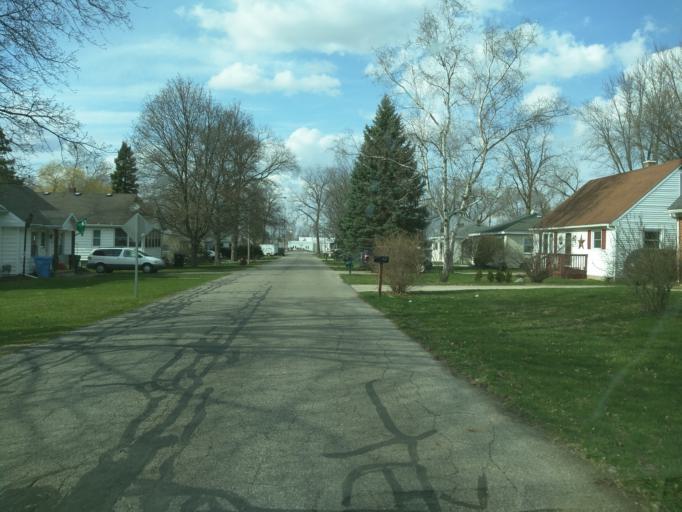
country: US
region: Michigan
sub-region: Ingham County
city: Edgemont Park
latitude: 42.7659
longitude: -84.5944
